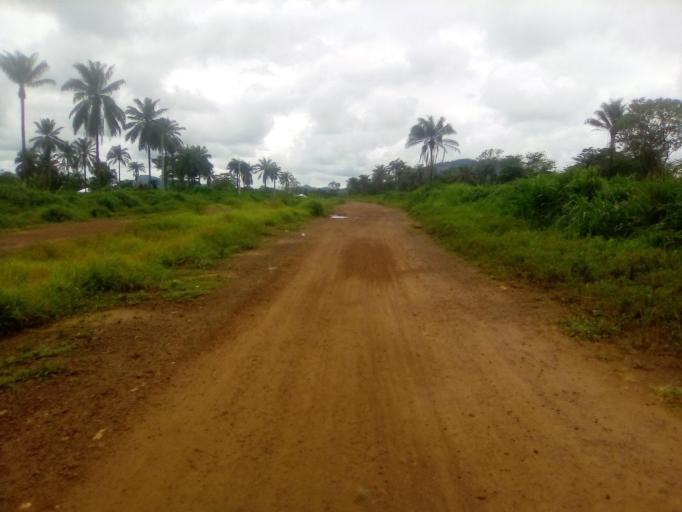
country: SL
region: Southern Province
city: Moyamba
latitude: 8.1454
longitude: -12.4391
